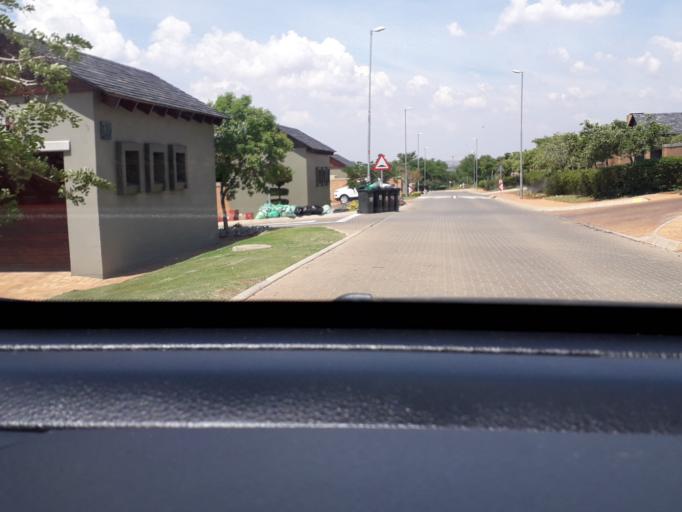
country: ZA
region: Gauteng
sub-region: City of Tshwane Metropolitan Municipality
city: Centurion
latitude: -25.9209
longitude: 28.1860
